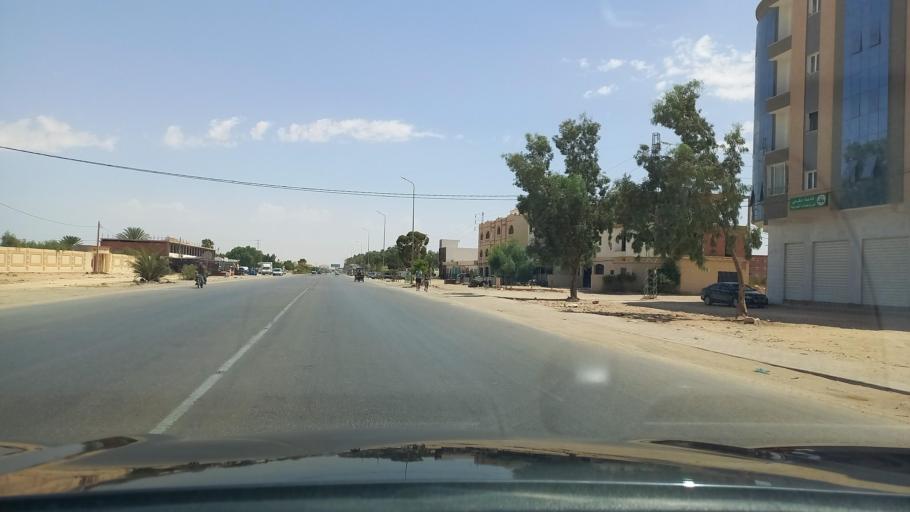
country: TN
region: Madanin
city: Medenine
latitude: 33.3643
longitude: 10.4609
